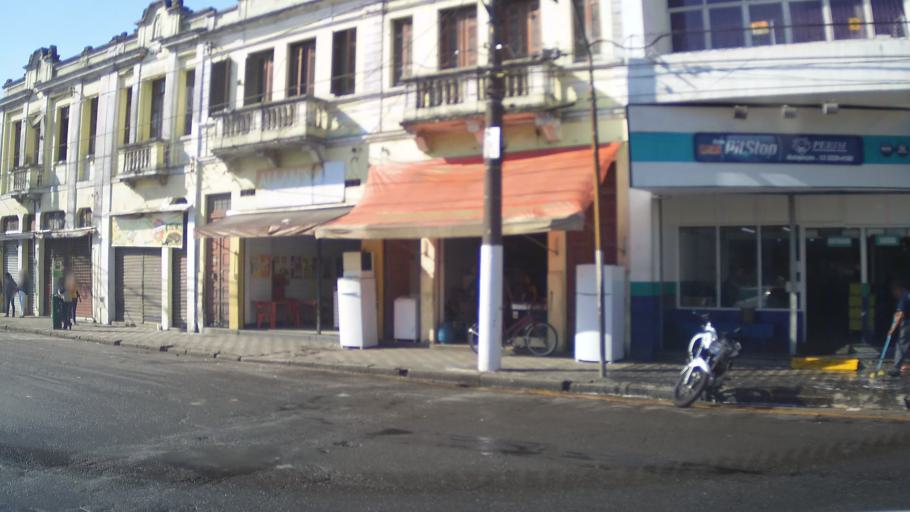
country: BR
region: Sao Paulo
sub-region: Santos
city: Santos
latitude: -23.9409
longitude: -46.3189
